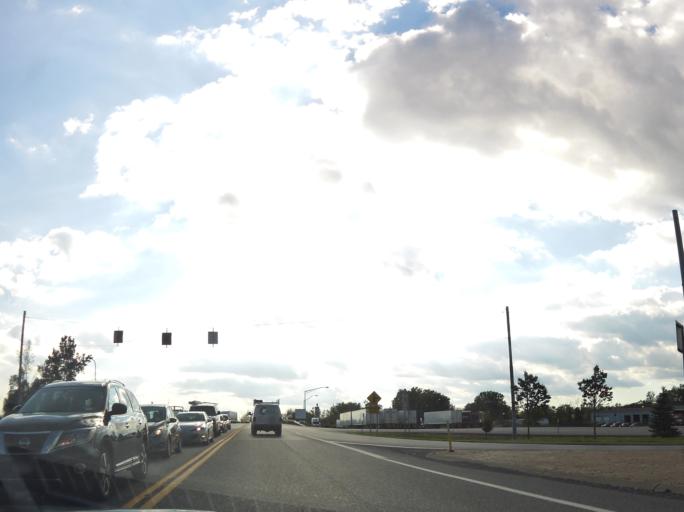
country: US
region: New York
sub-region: Erie County
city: Harris Hill
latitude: 42.9471
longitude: -78.6971
